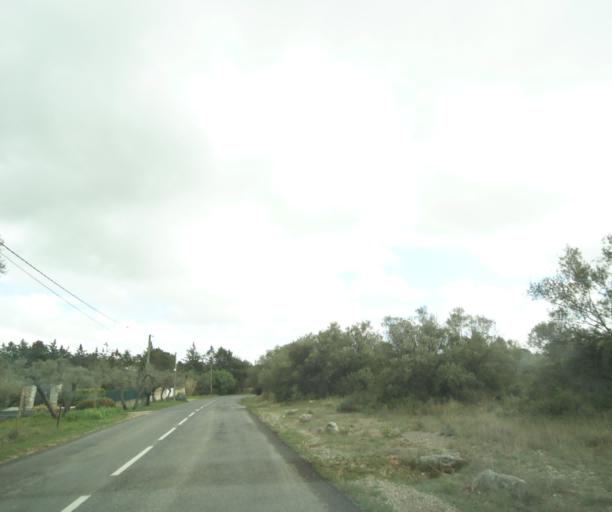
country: FR
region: Languedoc-Roussillon
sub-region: Departement de l'Herault
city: Pignan
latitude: 43.5934
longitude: 3.7499
